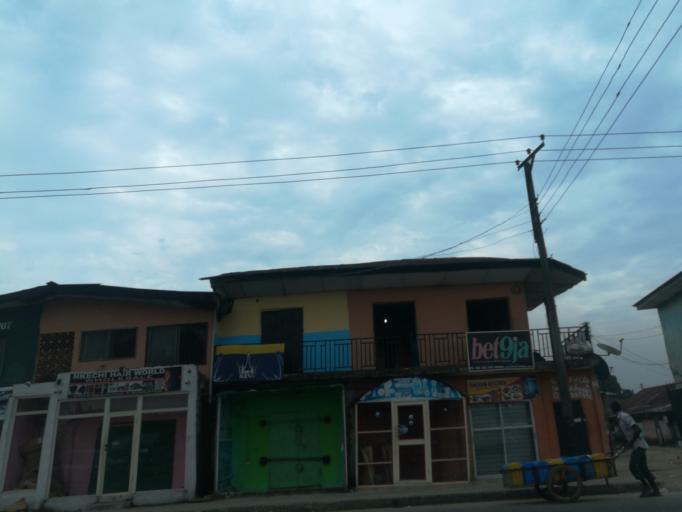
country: NG
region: Rivers
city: Port Harcourt
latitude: 4.8510
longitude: 6.9774
